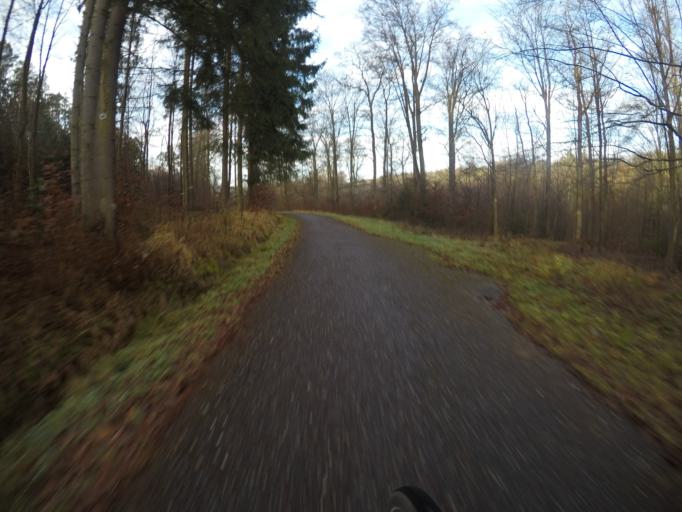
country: DE
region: Baden-Wuerttemberg
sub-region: Regierungsbezirk Stuttgart
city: Sindelfingen
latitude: 48.7247
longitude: 9.0369
